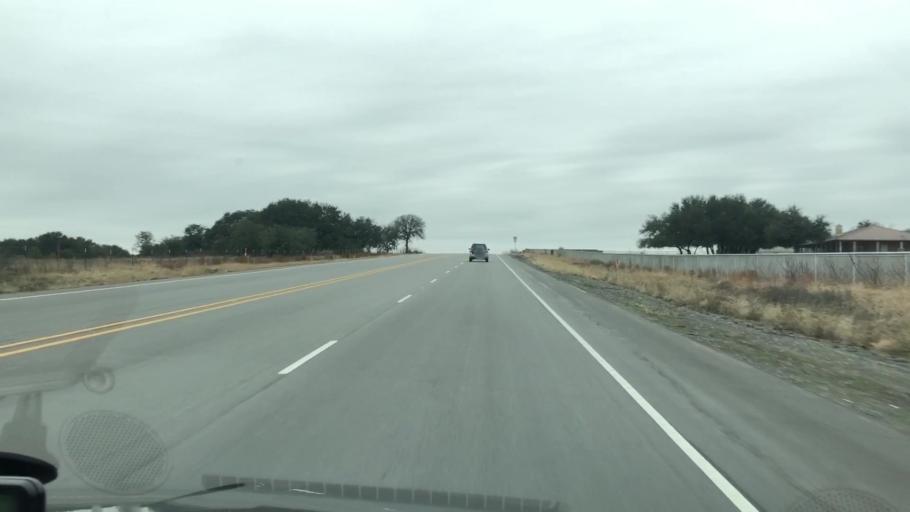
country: US
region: Texas
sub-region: Hamilton County
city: Hico
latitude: 32.0027
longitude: -98.0534
